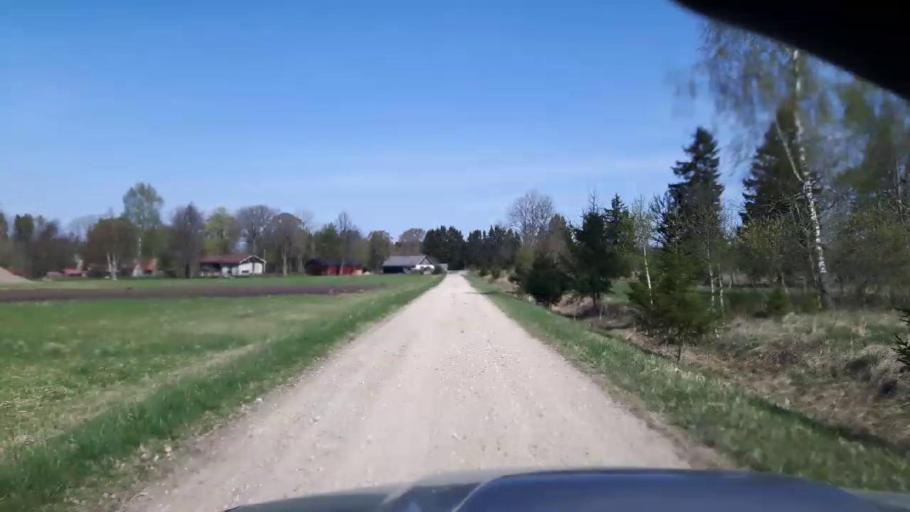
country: EE
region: Paernumaa
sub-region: Tootsi vald
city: Tootsi
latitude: 58.4958
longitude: 24.9294
